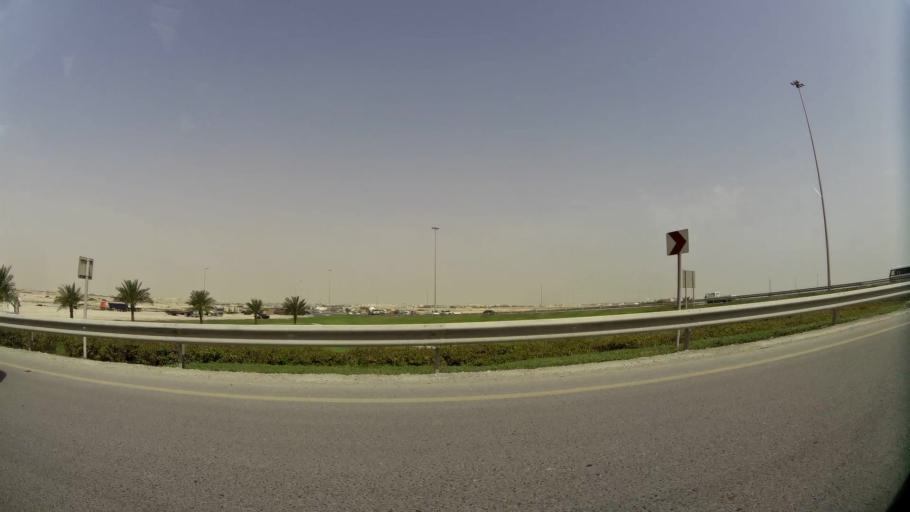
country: QA
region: Baladiyat ar Rayyan
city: Ar Rayyan
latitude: 25.2122
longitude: 51.4050
